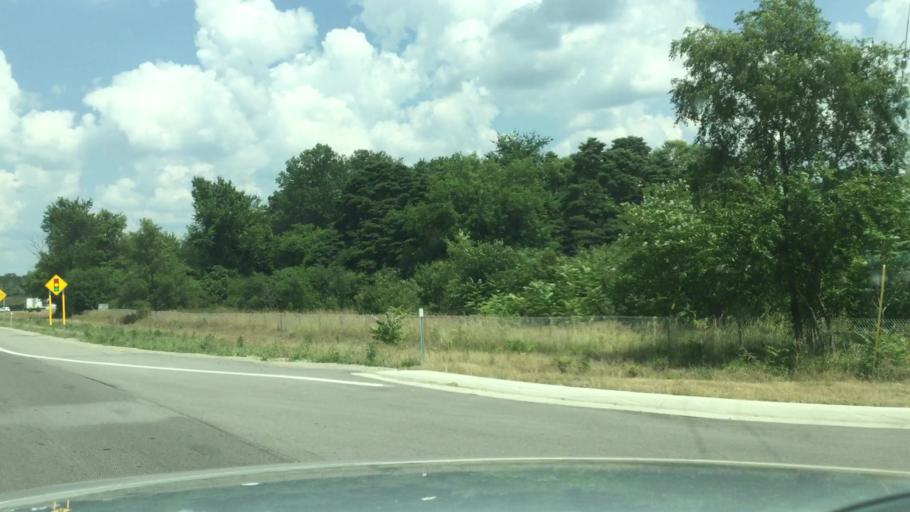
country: US
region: Michigan
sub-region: Washtenaw County
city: Ypsilanti
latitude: 42.2396
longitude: -83.5692
